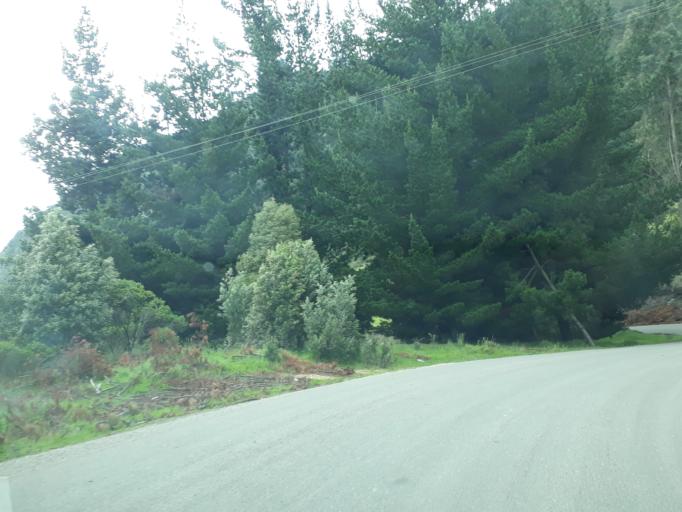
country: CO
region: Cundinamarca
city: Cucunuba
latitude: 5.2140
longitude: -73.7836
